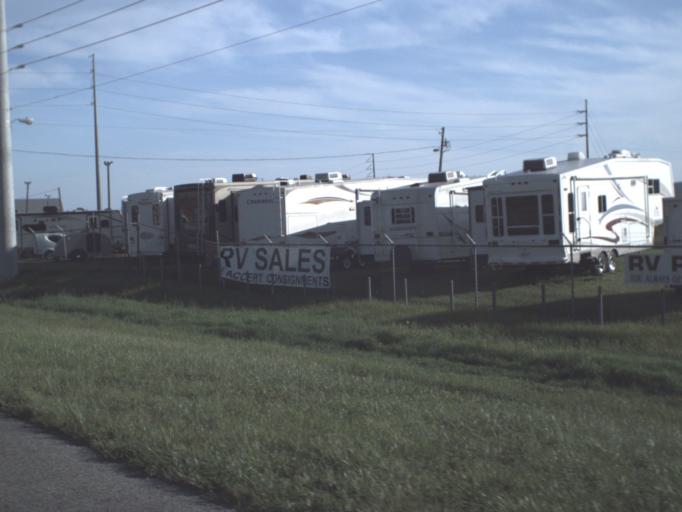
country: US
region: Florida
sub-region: Highlands County
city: Avon Park
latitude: 27.5498
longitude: -81.5077
